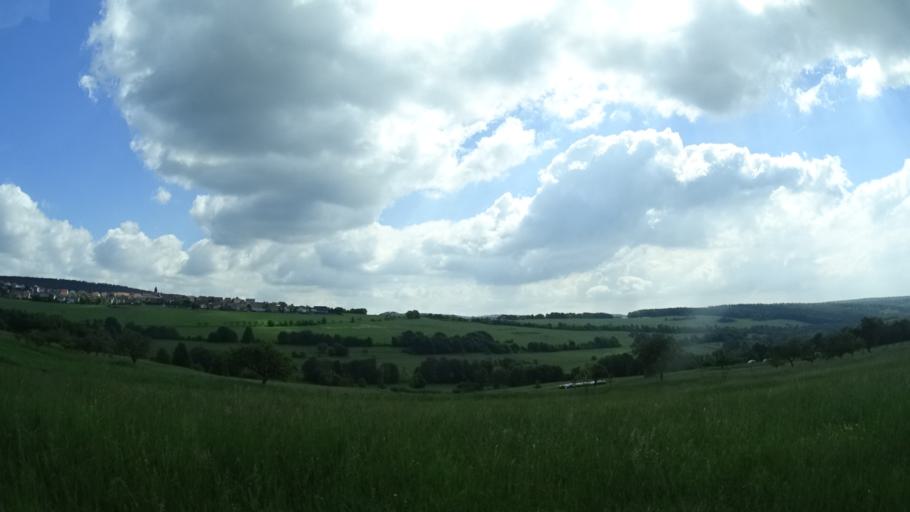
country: DE
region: Bavaria
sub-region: Regierungsbezirk Unterfranken
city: Sandberg
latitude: 50.3413
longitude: 9.9965
